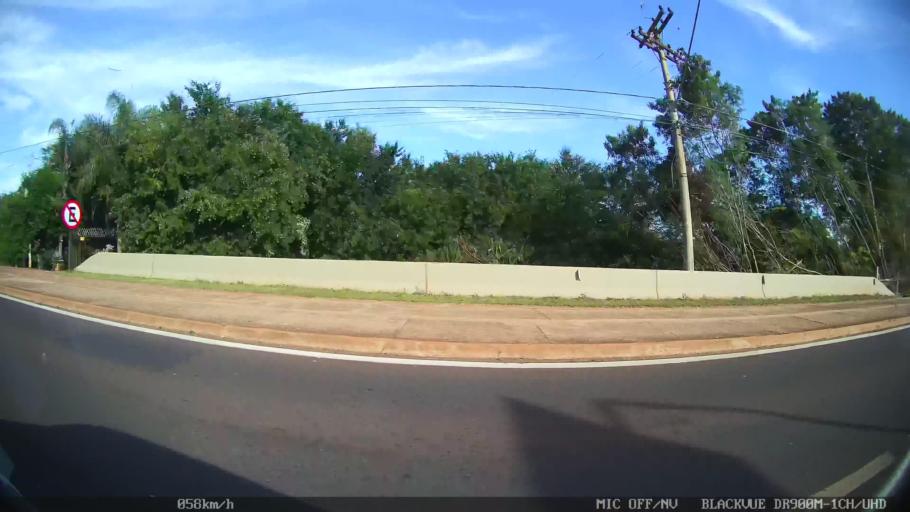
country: BR
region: Sao Paulo
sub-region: Araraquara
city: Araraquara
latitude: -21.7904
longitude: -48.1425
